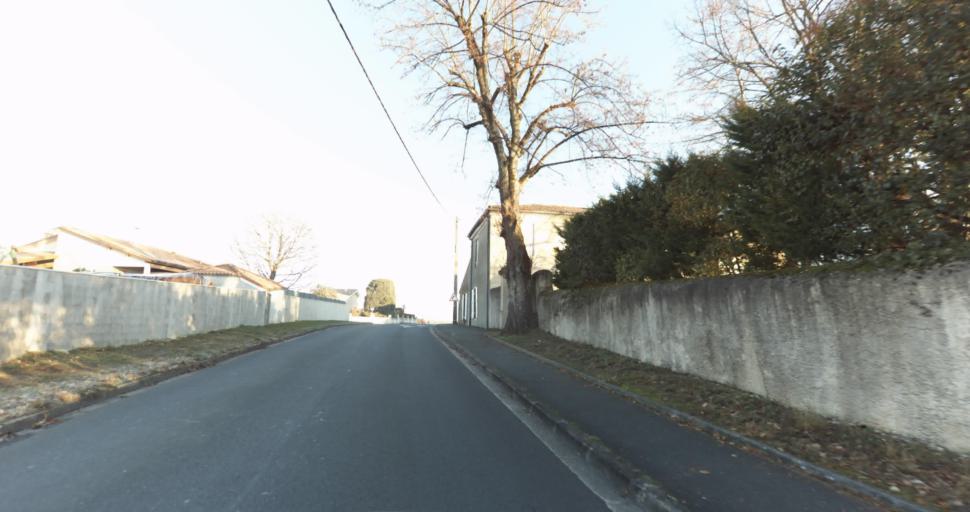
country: FR
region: Aquitaine
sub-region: Departement de la Gironde
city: Carbon-Blanc
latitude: 44.9092
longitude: -0.5029
